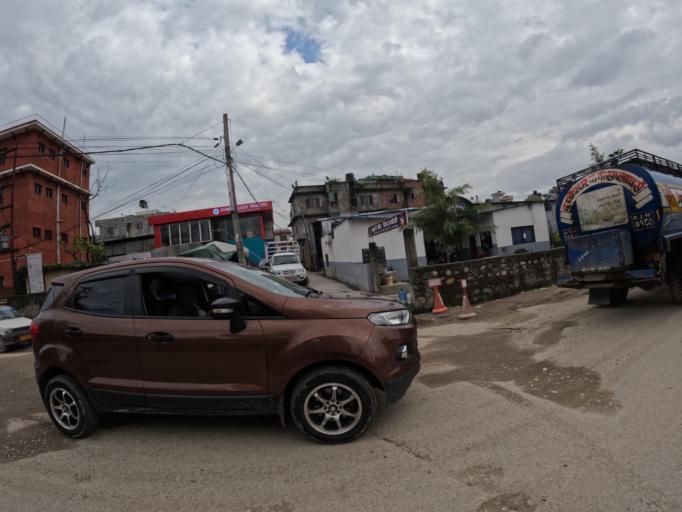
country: NP
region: Central Region
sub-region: Bagmati Zone
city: Kathmandu
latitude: 27.7394
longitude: 85.3108
